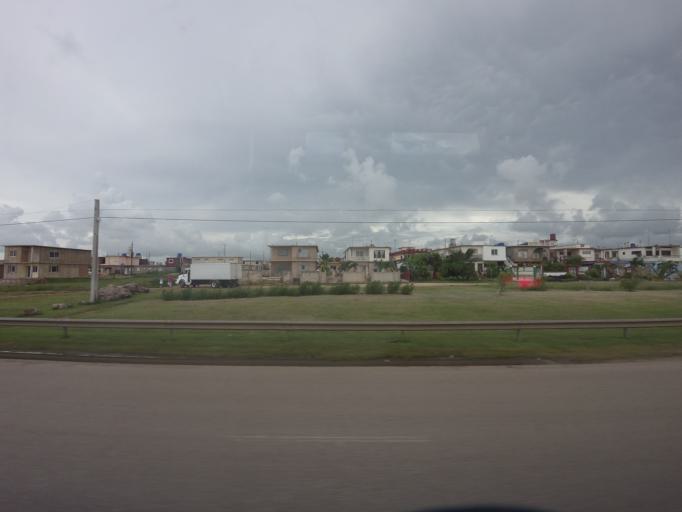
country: CU
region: Matanzas
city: Varadero
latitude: 23.1135
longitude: -81.3617
